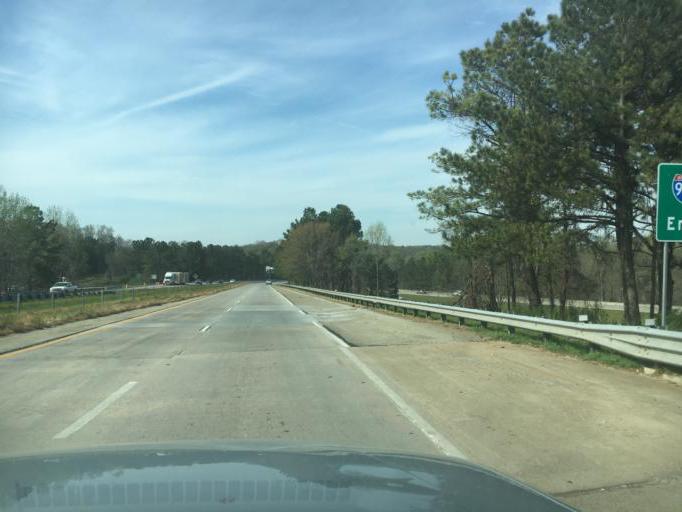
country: US
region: Georgia
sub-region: Hall County
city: Gainesville
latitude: 34.3163
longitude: -83.7885
